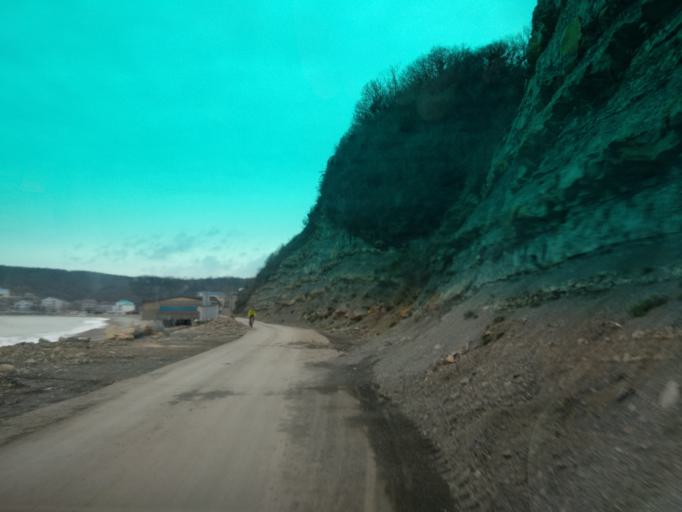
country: RU
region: Krasnodarskiy
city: Novomikhaylovskiy
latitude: 44.2357
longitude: 38.8387
